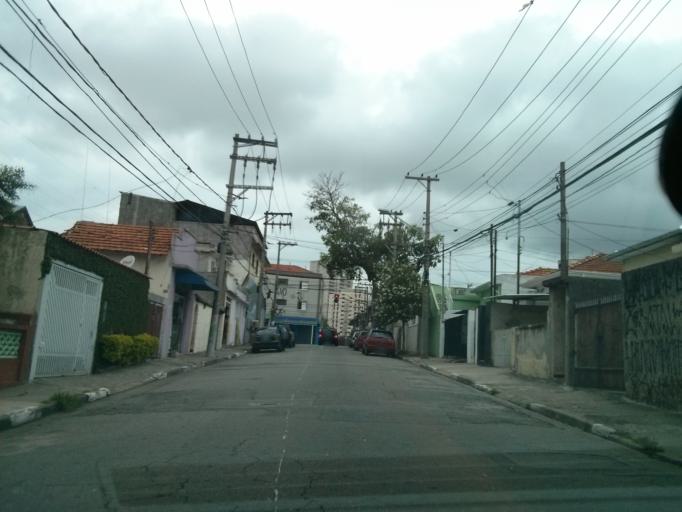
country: BR
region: Sao Paulo
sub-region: Sao Paulo
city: Sao Paulo
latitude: -23.6083
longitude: -46.6176
